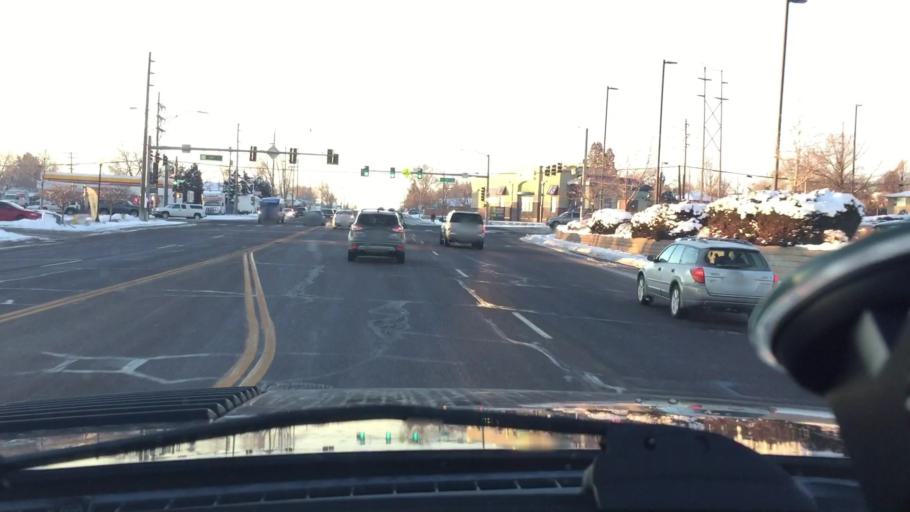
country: US
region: Colorado
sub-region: Adams County
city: Federal Heights
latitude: 39.8498
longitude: -105.0061
